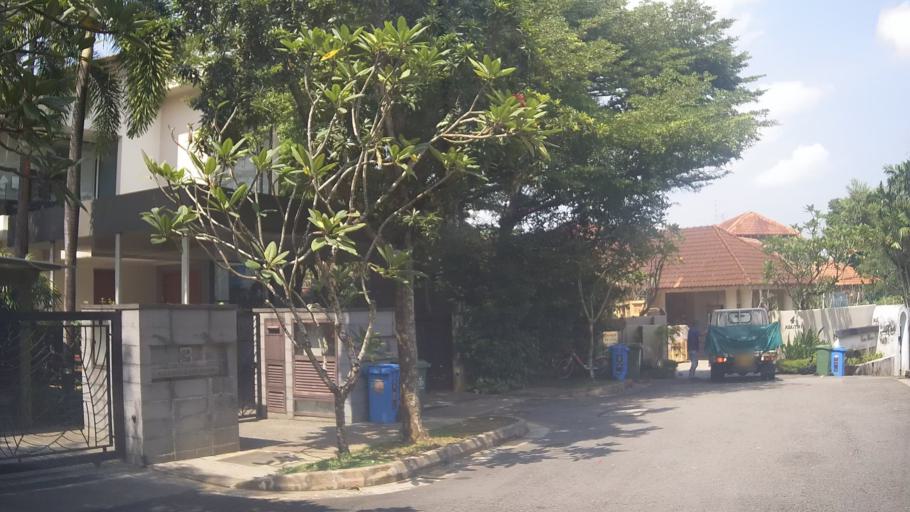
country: SG
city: Singapore
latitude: 1.3191
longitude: 103.8028
